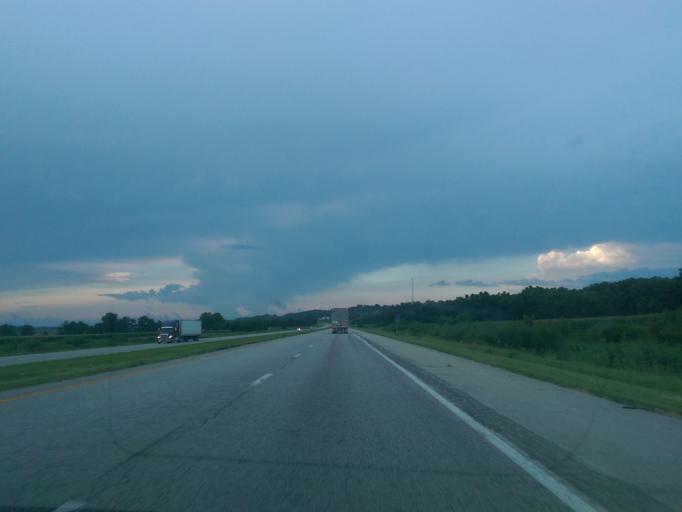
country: US
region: Missouri
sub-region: Holt County
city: Mound City
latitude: 40.0872
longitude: -95.2120
